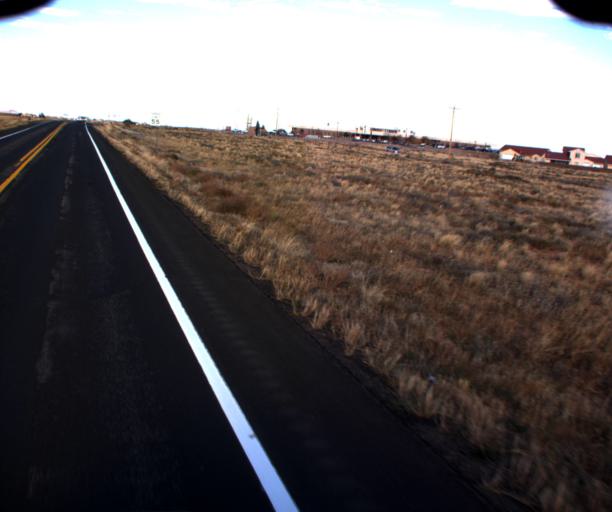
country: US
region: Arizona
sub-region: Apache County
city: Lukachukai
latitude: 36.9596
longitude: -109.3443
